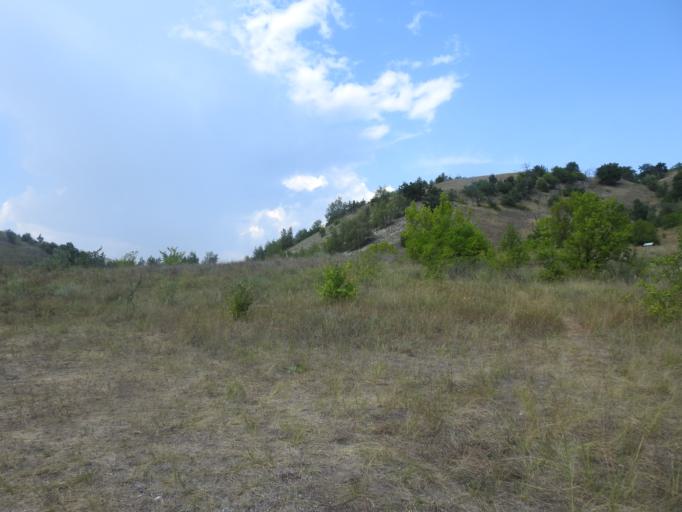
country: RU
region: Saratov
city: Kamenskiy
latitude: 50.4927
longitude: 45.7022
